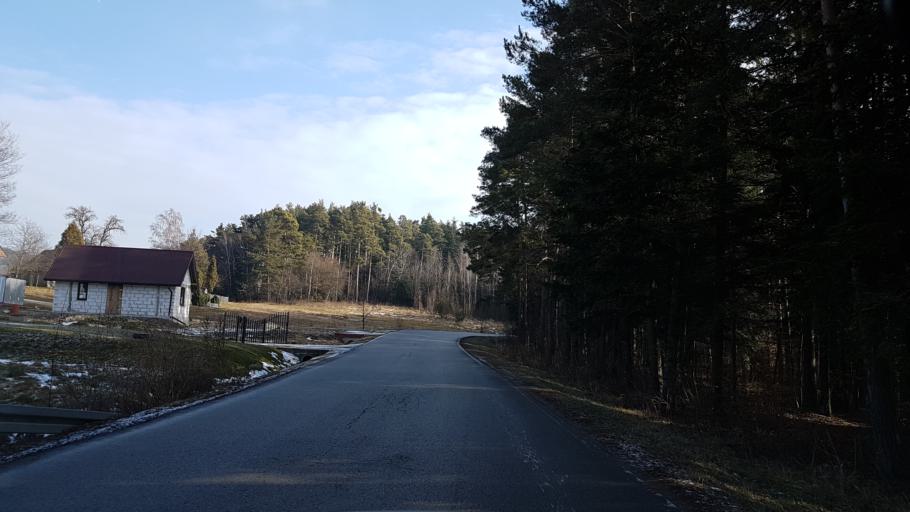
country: PL
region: Lesser Poland Voivodeship
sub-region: Powiat limanowski
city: Lukowica
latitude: 49.6366
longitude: 20.5160
